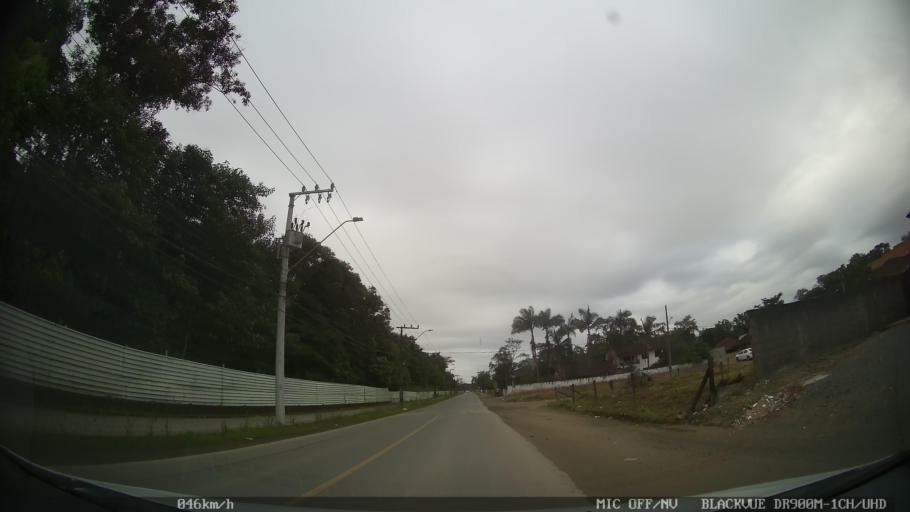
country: BR
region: Santa Catarina
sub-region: Joinville
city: Joinville
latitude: -26.2634
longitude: -48.9245
